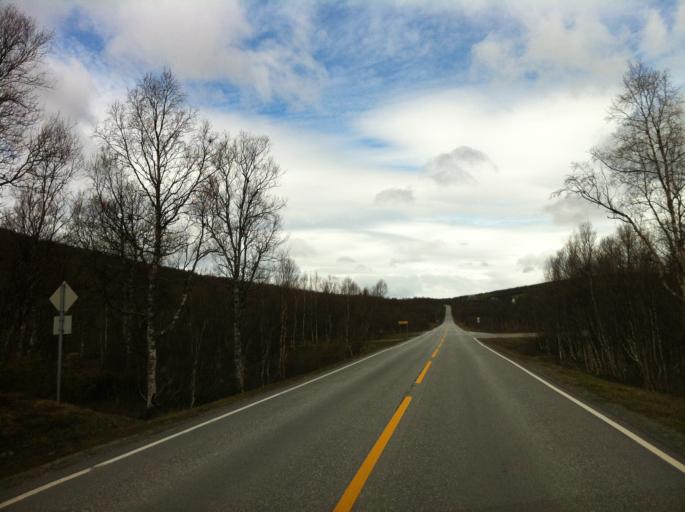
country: NO
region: Sor-Trondelag
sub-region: Roros
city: Roros
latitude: 62.5911
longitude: 11.7840
